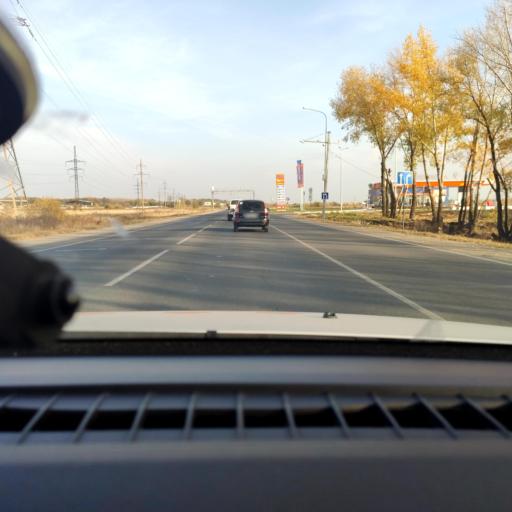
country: RU
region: Samara
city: Samara
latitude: 53.1297
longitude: 50.1531
